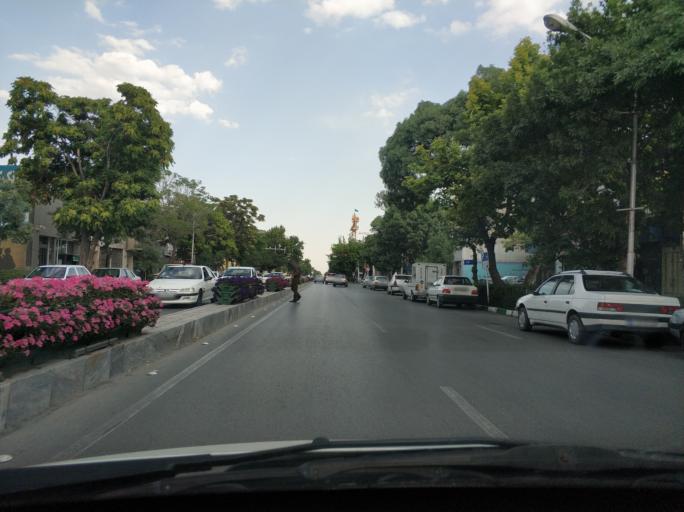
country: IR
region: Razavi Khorasan
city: Mashhad
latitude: 36.2804
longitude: 59.5966
